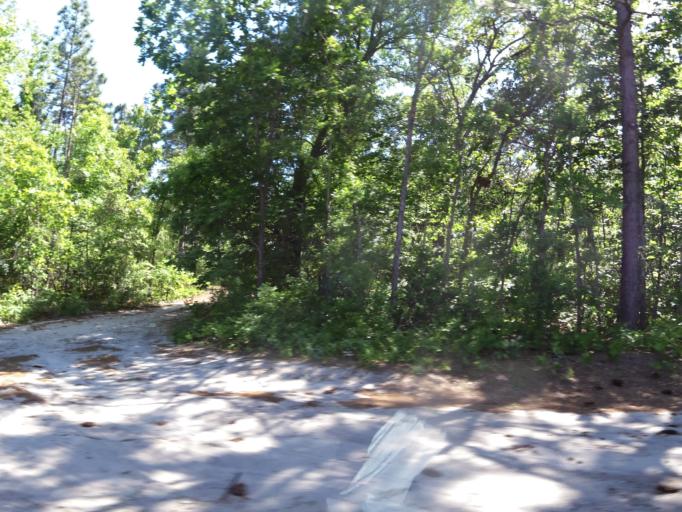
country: US
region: South Carolina
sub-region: Barnwell County
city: Williston
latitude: 33.5054
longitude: -81.5442
